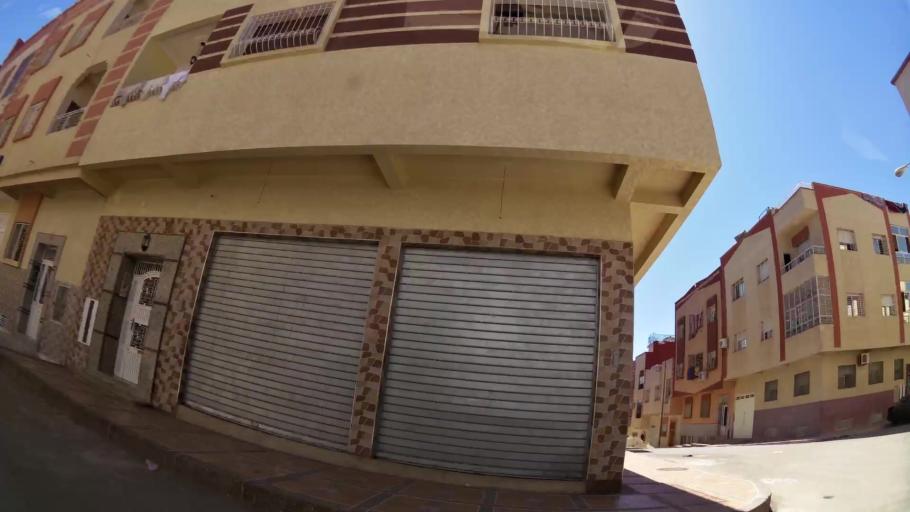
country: MA
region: Meknes-Tafilalet
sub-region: Meknes
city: Meknes
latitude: 33.8986
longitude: -5.5817
